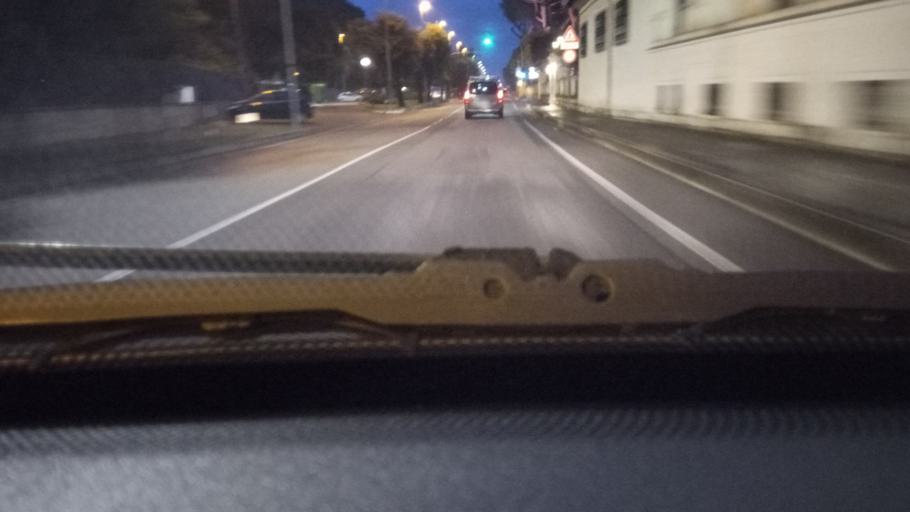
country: IT
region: Latium
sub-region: Provincia di Latina
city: Formia
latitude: 41.2616
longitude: 13.6288
